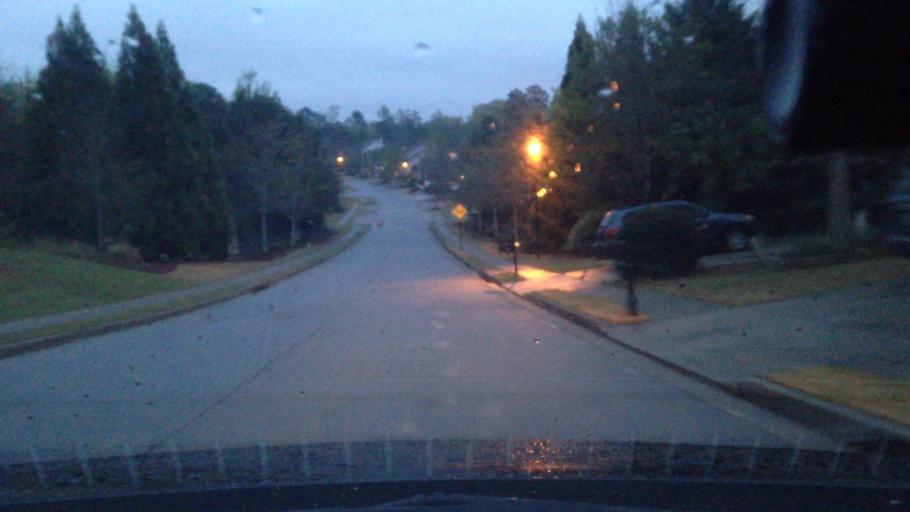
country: US
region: Georgia
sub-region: Coweta County
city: East Newnan
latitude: 33.3813
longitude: -84.7467
